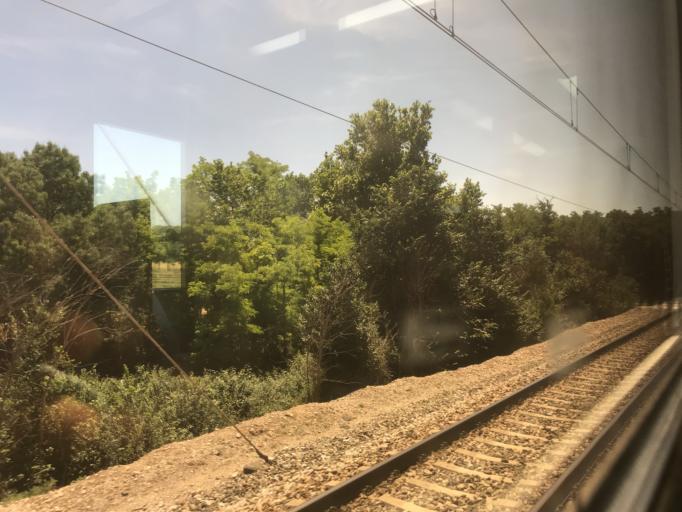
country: ES
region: Madrid
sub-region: Provincia de Madrid
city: Aranjuez
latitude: 40.0445
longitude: -3.6214
